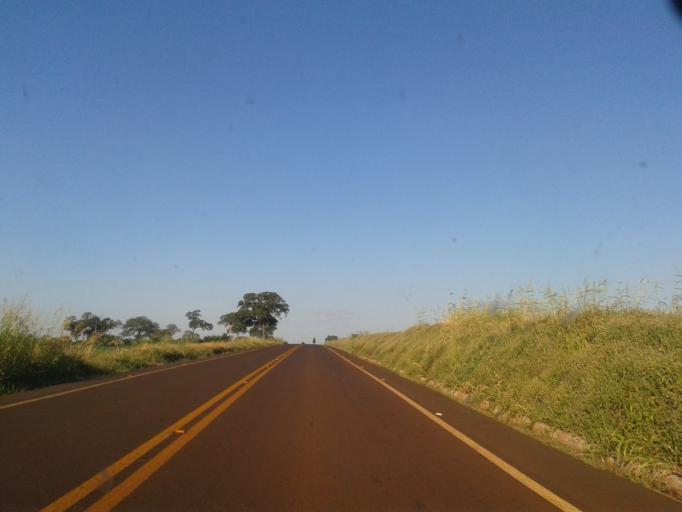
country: BR
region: Minas Gerais
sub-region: Capinopolis
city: Capinopolis
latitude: -18.7120
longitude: -49.7782
